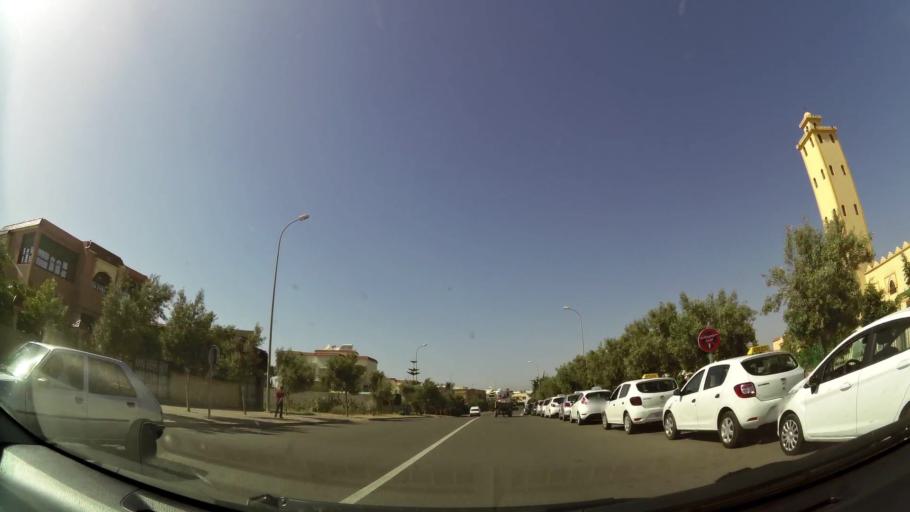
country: MA
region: Souss-Massa-Draa
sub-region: Inezgane-Ait Mellou
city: Inezgane
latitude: 30.3600
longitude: -9.5499
